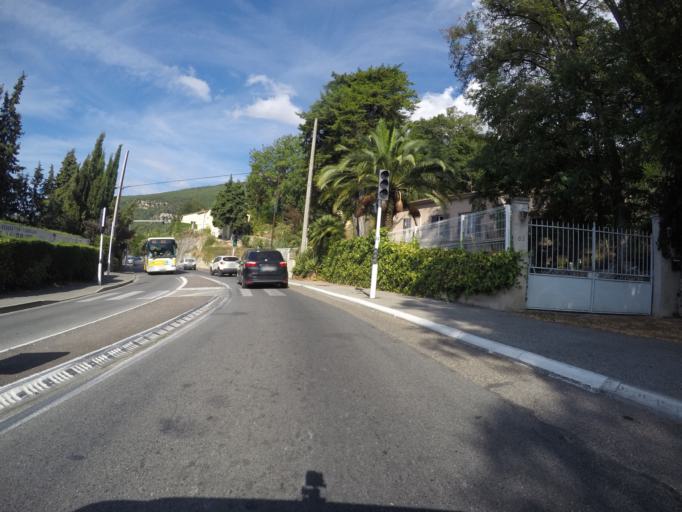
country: FR
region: Provence-Alpes-Cote d'Azur
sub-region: Departement des Alpes-Maritimes
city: Opio
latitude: 43.6818
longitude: 6.9558
